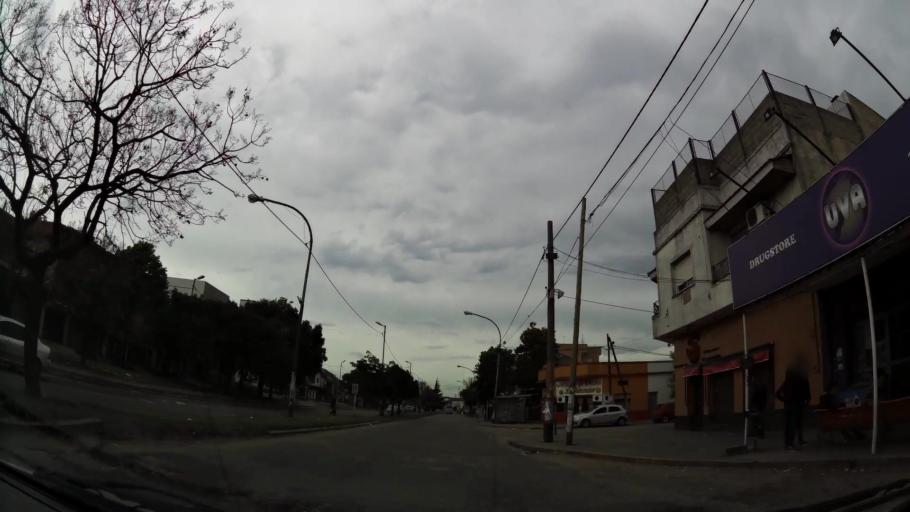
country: AR
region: Buenos Aires
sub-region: Partido de Quilmes
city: Quilmes
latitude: -34.7903
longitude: -58.2789
